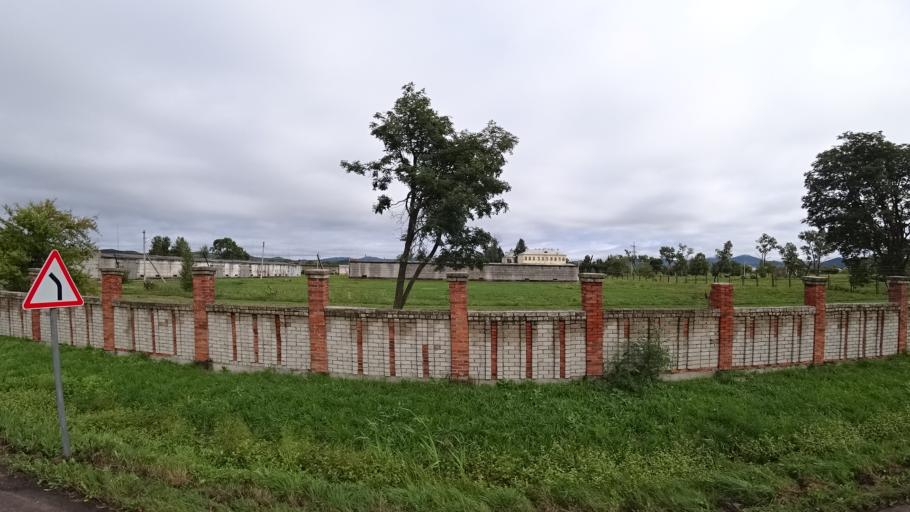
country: RU
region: Primorskiy
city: Monastyrishche
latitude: 44.2032
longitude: 132.4747
